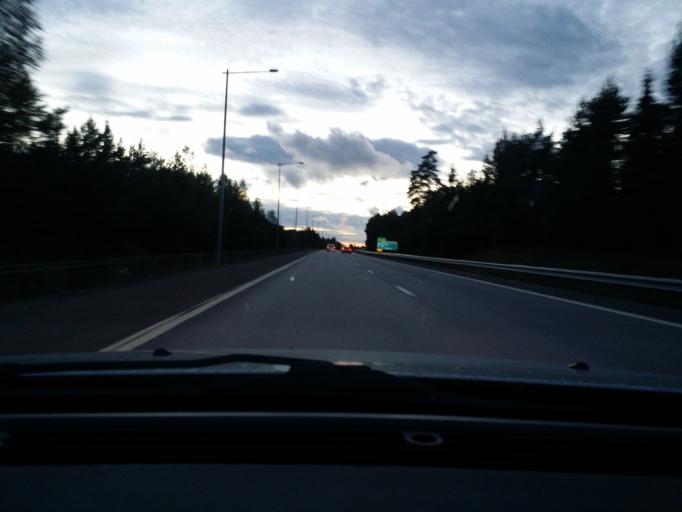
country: SE
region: Stockholm
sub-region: Upplands-Bro Kommun
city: Bro
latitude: 59.5245
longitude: 17.6523
